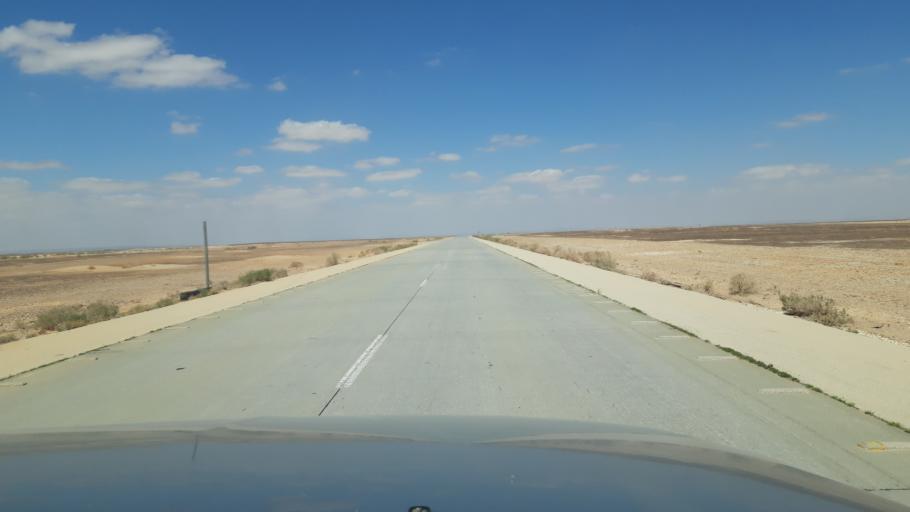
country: JO
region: Amman
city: Al Azraq ash Shamali
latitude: 31.5739
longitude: 36.8244
